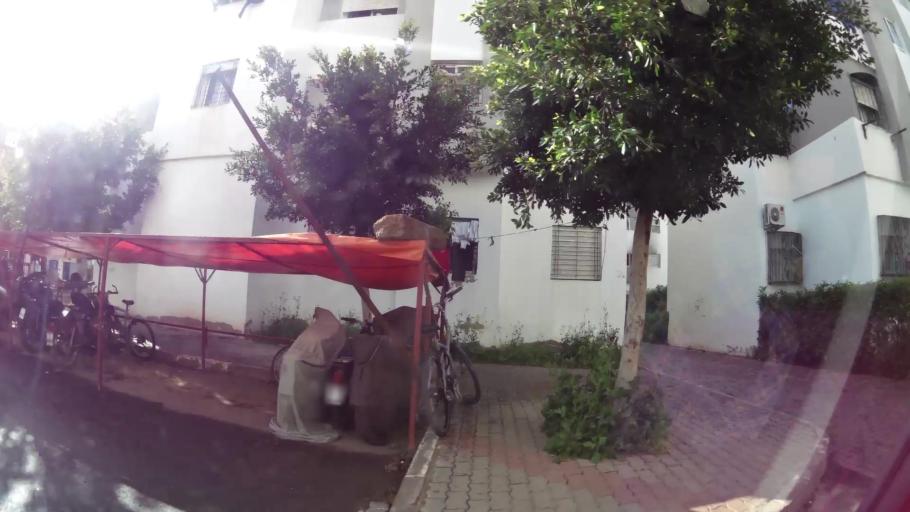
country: MA
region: Grand Casablanca
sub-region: Casablanca
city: Casablanca
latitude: 33.5557
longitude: -7.7018
